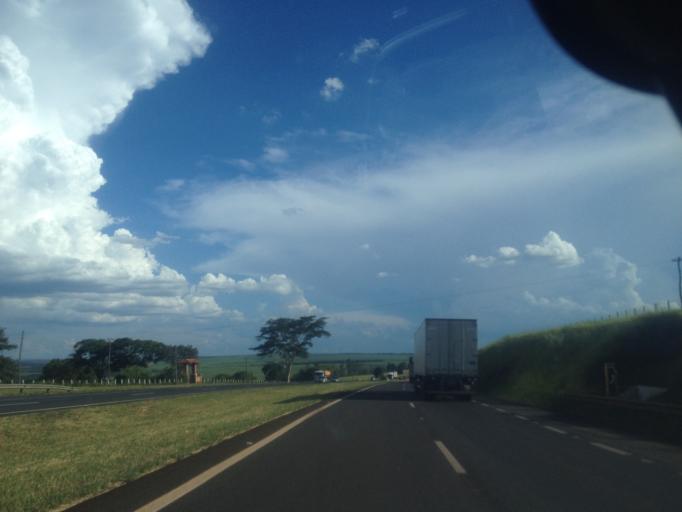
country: BR
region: Sao Paulo
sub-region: Sao Simao
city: Sao Simao
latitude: -21.4704
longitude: -47.6407
